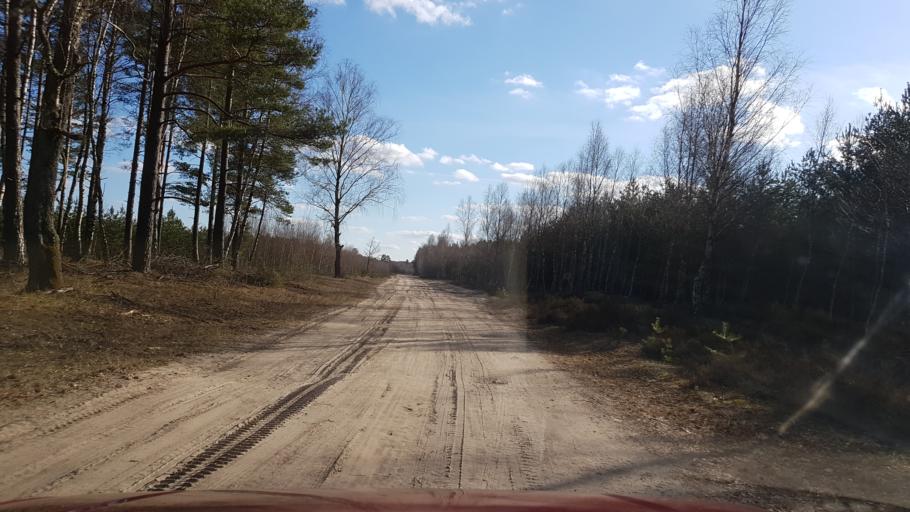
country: PL
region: Greater Poland Voivodeship
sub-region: Powiat zlotowski
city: Sypniewo
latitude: 53.5334
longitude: 16.6462
